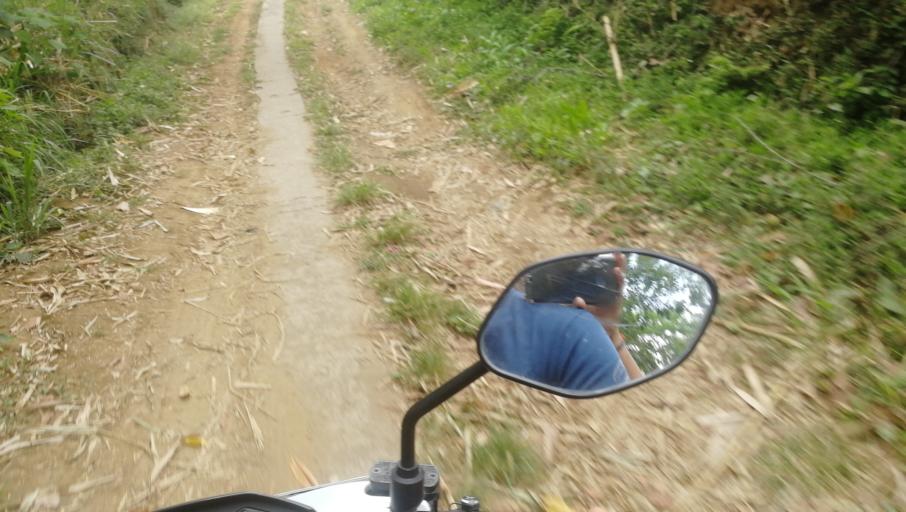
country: ID
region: Bali
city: Munduk
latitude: -8.3086
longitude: 115.0590
